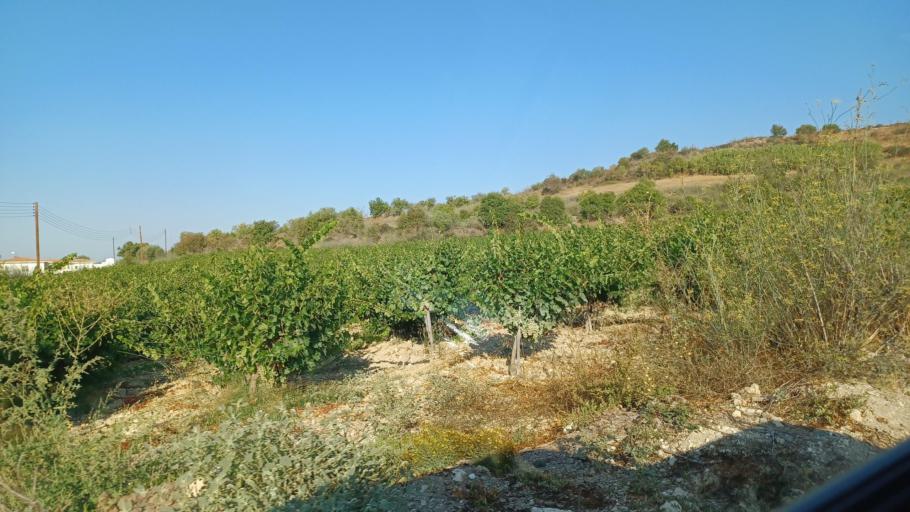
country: CY
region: Pafos
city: Tala
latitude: 34.8945
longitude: 32.5033
